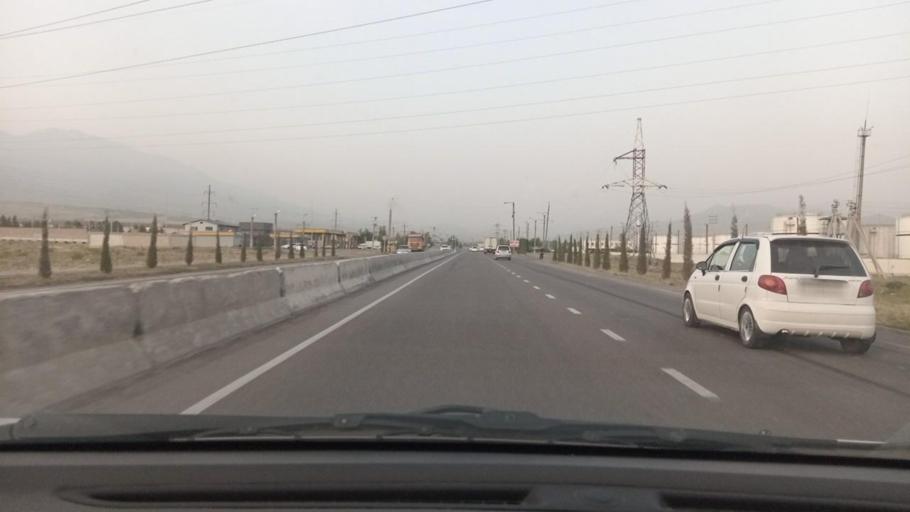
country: UZ
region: Toshkent
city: Angren
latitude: 41.0170
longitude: 70.1132
